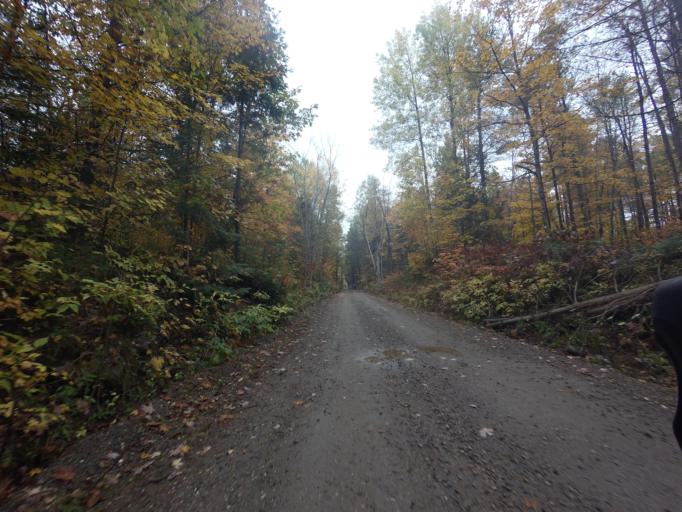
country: CA
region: Ontario
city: Renfrew
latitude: 45.1841
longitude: -76.6852
